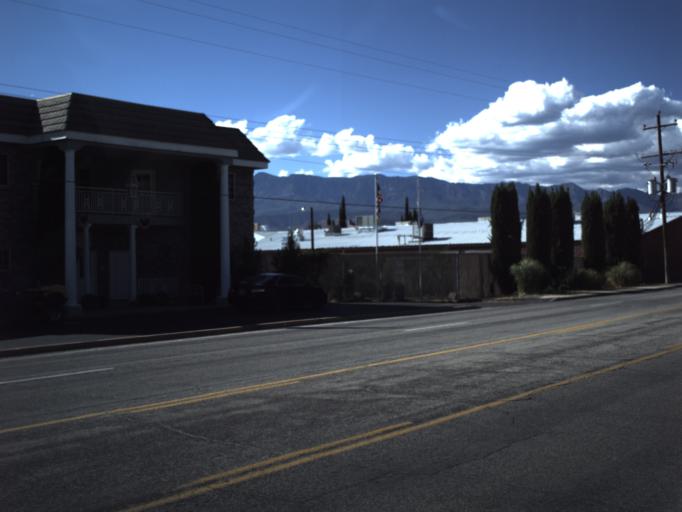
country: US
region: Utah
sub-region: Washington County
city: LaVerkin
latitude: 37.2124
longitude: -113.2721
